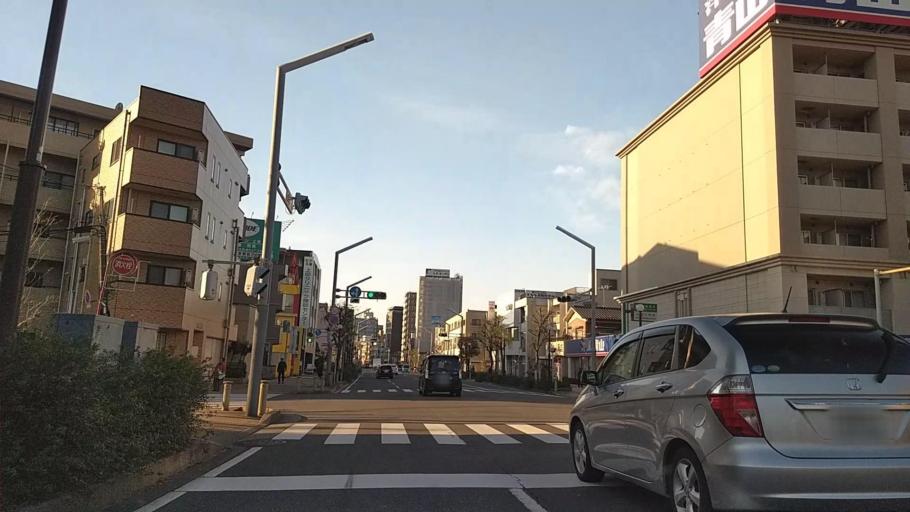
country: JP
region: Tokyo
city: Urayasu
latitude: 35.6625
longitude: 139.8985
